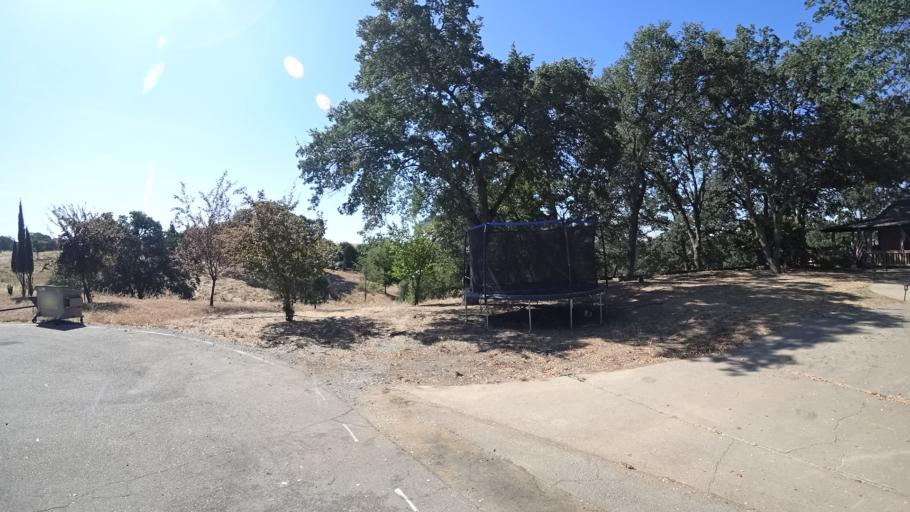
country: US
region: California
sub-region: Calaveras County
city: Rancho Calaveras
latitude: 38.0987
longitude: -120.8755
